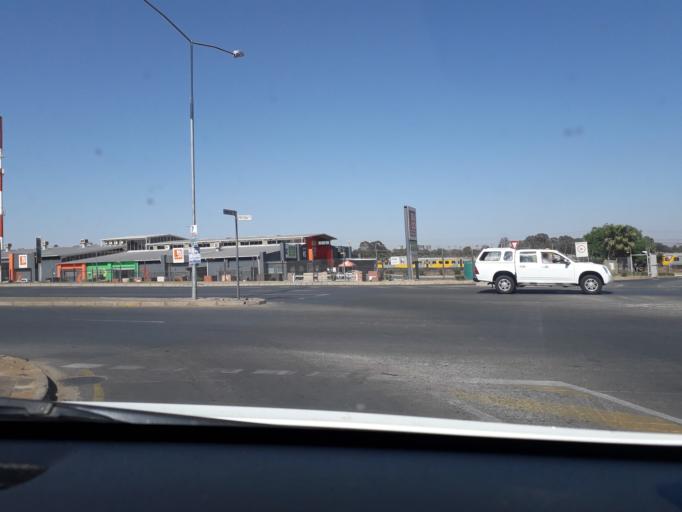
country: ZA
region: Gauteng
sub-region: City of Johannesburg Metropolitan Municipality
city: Modderfontein
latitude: -26.0983
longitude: 28.2233
